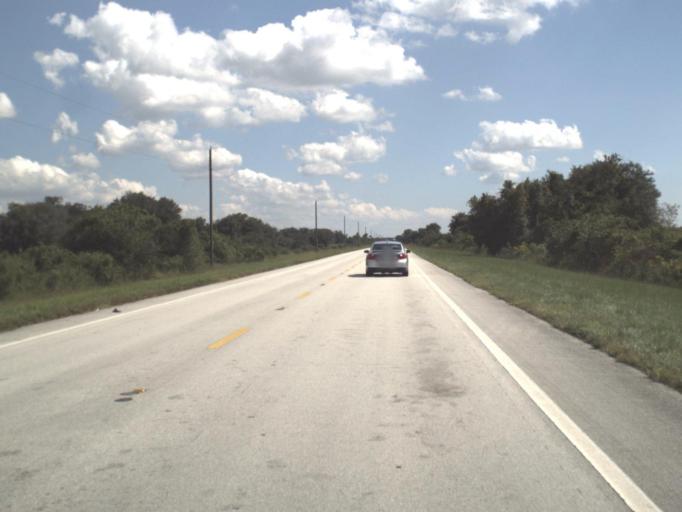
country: US
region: Florida
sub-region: Highlands County
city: Lake Placid
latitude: 27.3928
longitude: -81.1498
